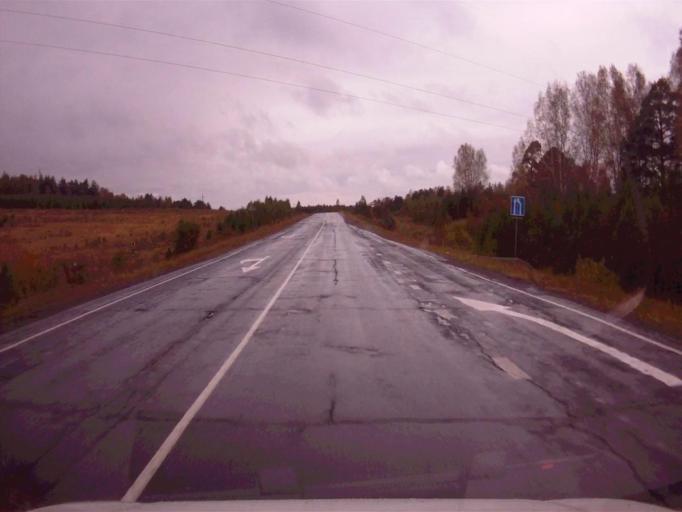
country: RU
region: Chelyabinsk
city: Verkhniy Ufaley
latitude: 56.0065
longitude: 60.3261
